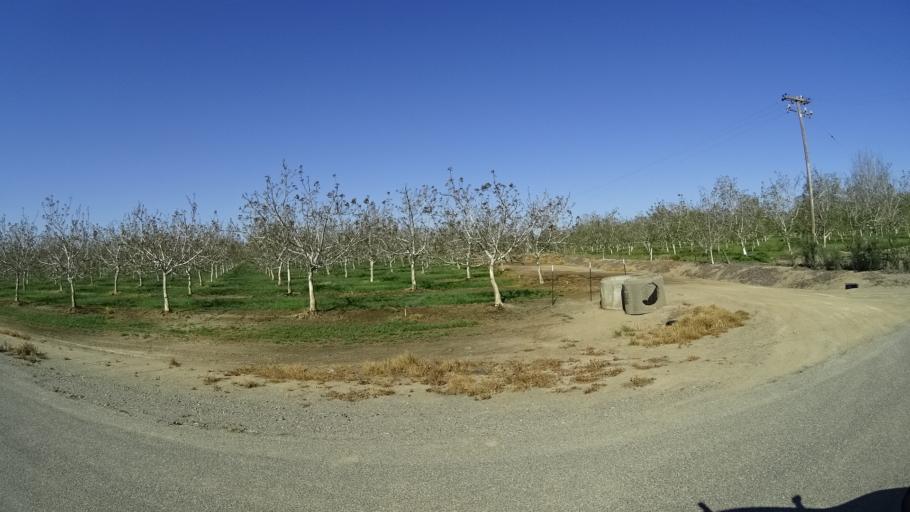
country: US
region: California
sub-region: Glenn County
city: Hamilton City
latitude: 39.6922
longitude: -122.0743
